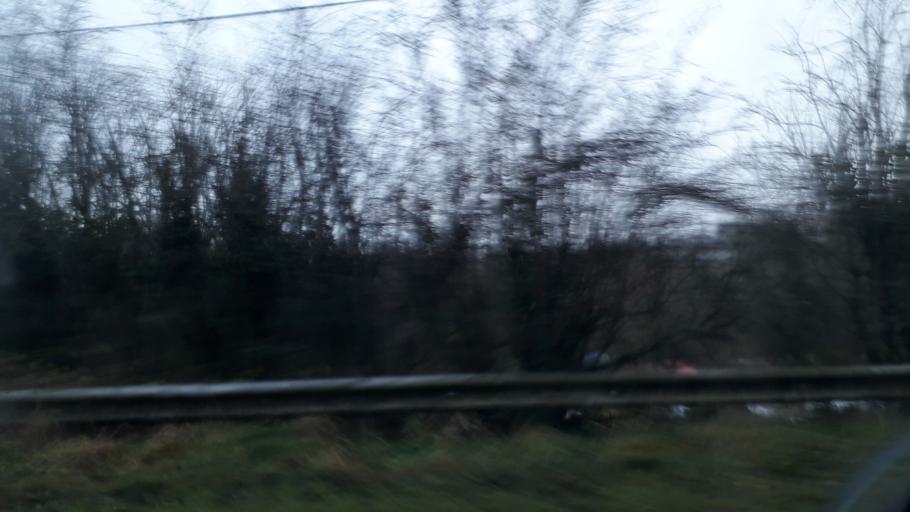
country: IE
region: Ulster
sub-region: County Donegal
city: Raphoe
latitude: 54.9377
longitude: -7.6152
